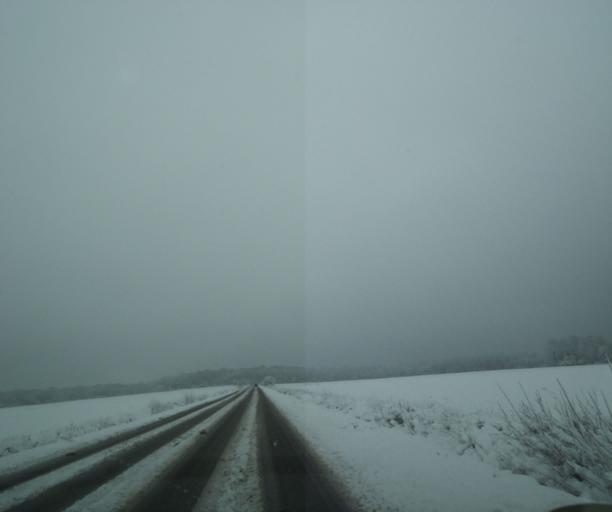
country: FR
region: Champagne-Ardenne
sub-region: Departement de la Haute-Marne
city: Saint-Dizier
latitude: 48.5957
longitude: 4.9064
